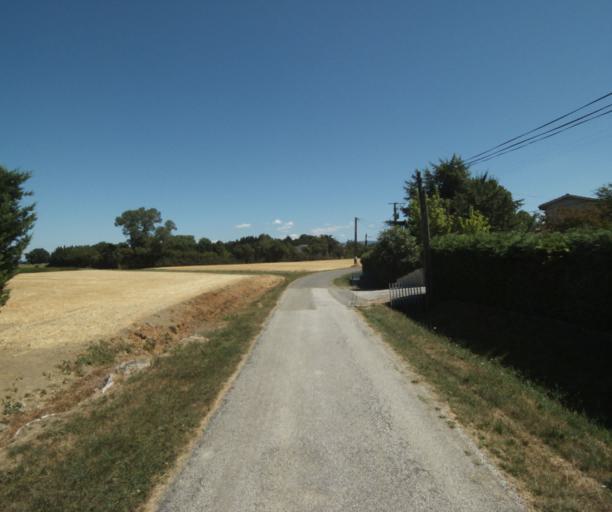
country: FR
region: Midi-Pyrenees
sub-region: Departement de la Haute-Garonne
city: Saint-Felix-Lauragais
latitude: 43.4790
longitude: 1.9390
